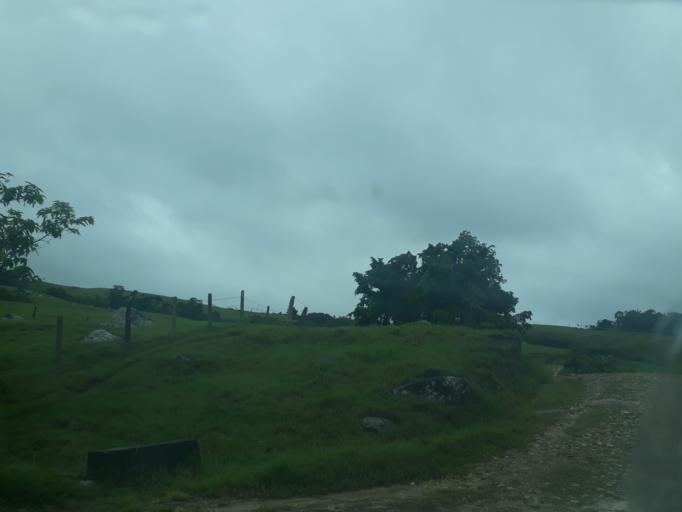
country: CO
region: Cundinamarca
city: Medina
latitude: 4.5337
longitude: -73.3883
